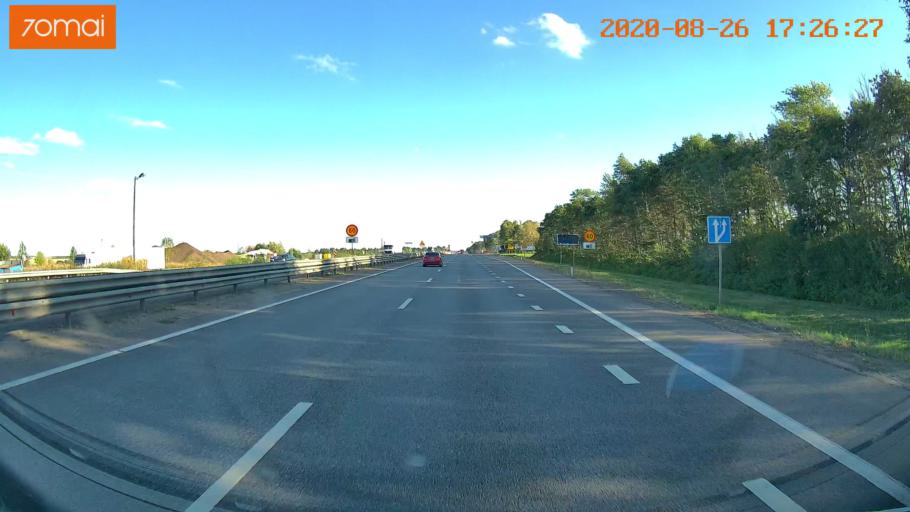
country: RU
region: Tula
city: Kazachka
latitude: 53.4867
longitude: 38.1171
